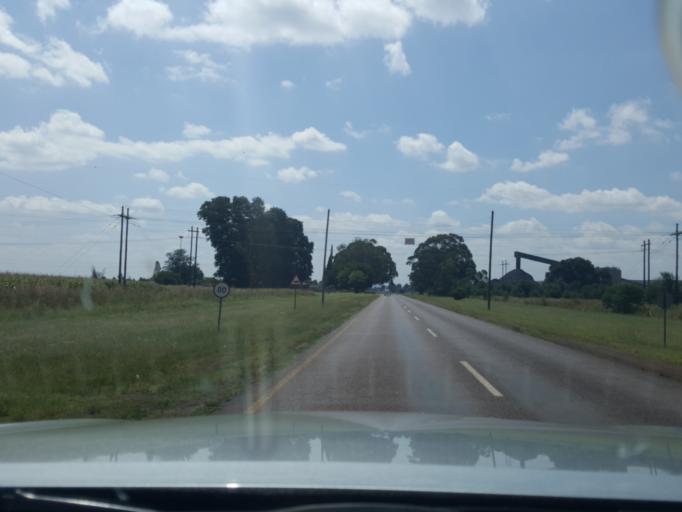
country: ZA
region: Mpumalanga
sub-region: Nkangala District Municipality
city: Middelburg
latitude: -25.9830
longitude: 29.4527
